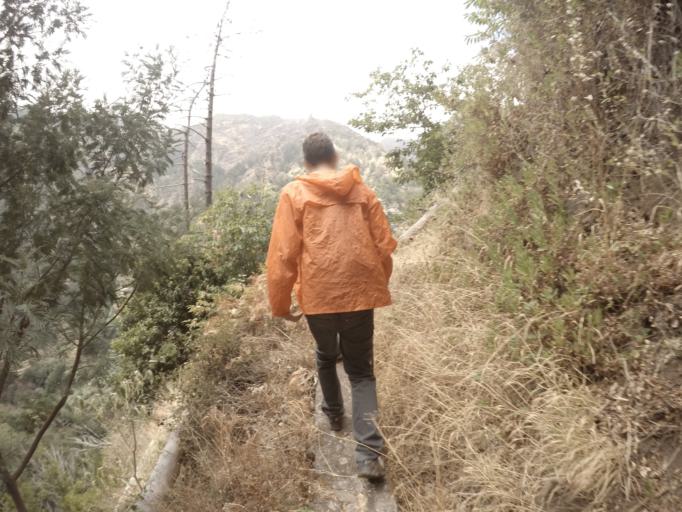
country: PT
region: Madeira
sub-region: Camara de Lobos
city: Curral das Freiras
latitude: 32.7073
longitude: -16.9684
